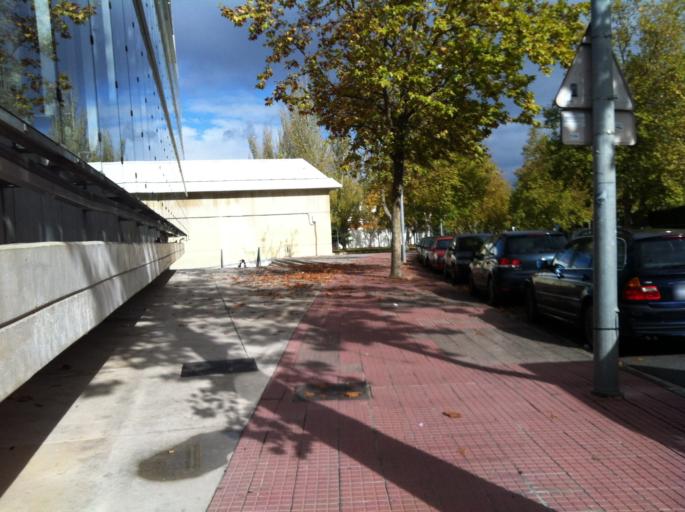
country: ES
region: Basque Country
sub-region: Provincia de Alava
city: Gasteiz / Vitoria
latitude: 42.8361
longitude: -2.6861
